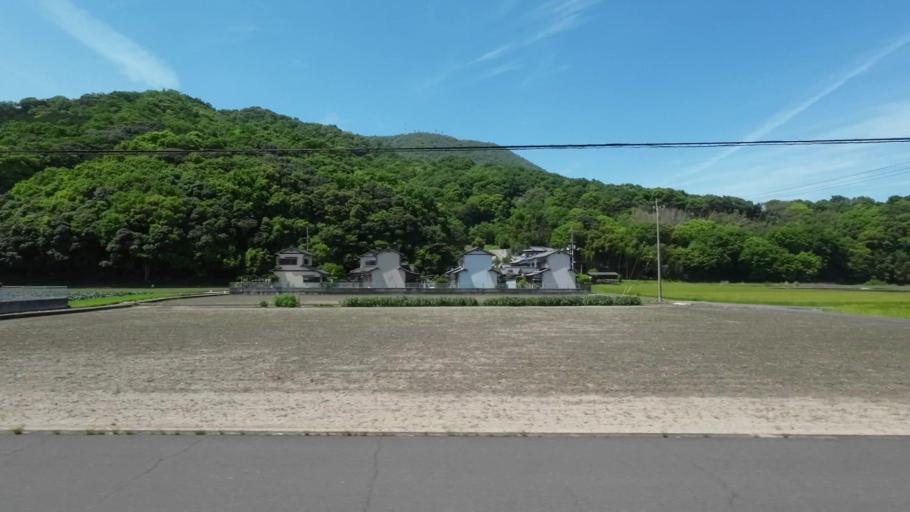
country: JP
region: Kagawa
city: Marugame
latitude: 34.2071
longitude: 133.8060
